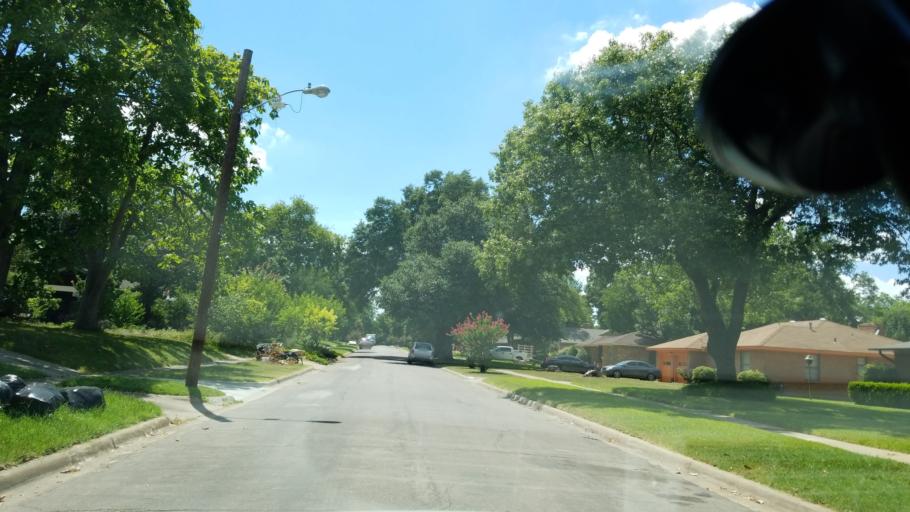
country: US
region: Texas
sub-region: Dallas County
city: Cockrell Hill
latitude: 32.7011
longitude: -96.8653
